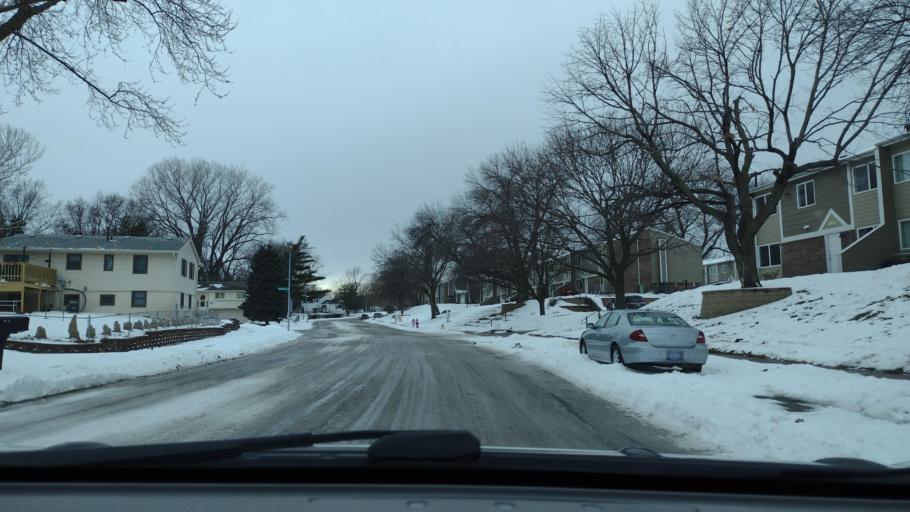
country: US
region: Nebraska
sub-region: Sarpy County
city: Offutt Air Force Base
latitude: 41.1796
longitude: -95.9340
